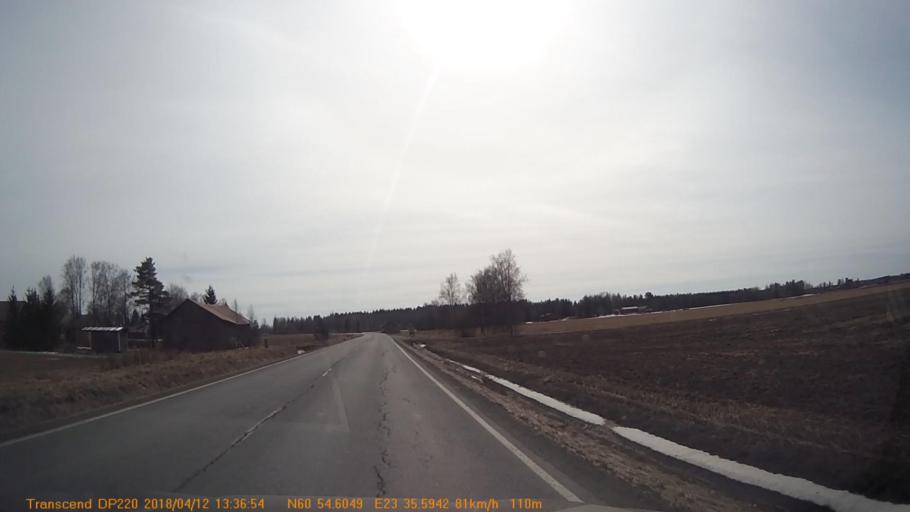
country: FI
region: Haeme
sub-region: Forssa
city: Forssa
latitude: 60.9098
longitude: 23.5932
